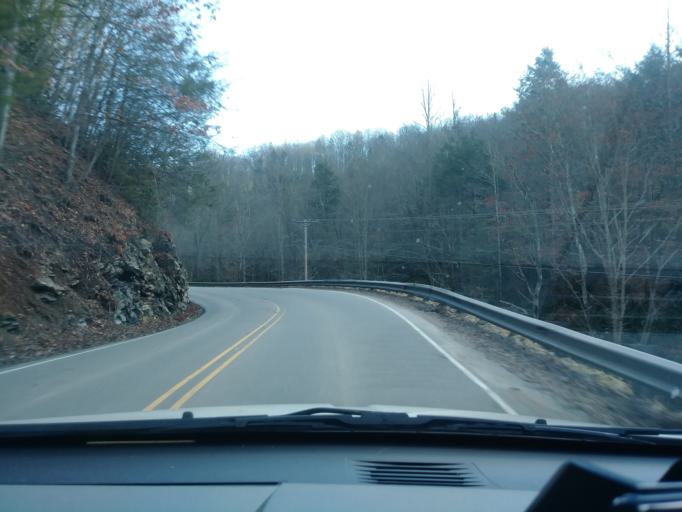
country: US
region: North Carolina
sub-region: Avery County
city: Newland
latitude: 36.1588
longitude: -81.9630
